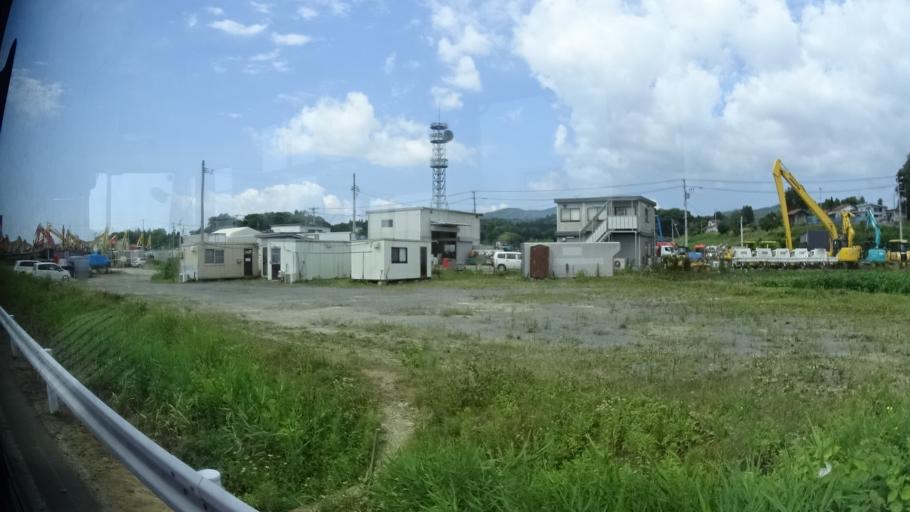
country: JP
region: Iwate
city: Ofunato
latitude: 38.8532
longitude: 141.5813
